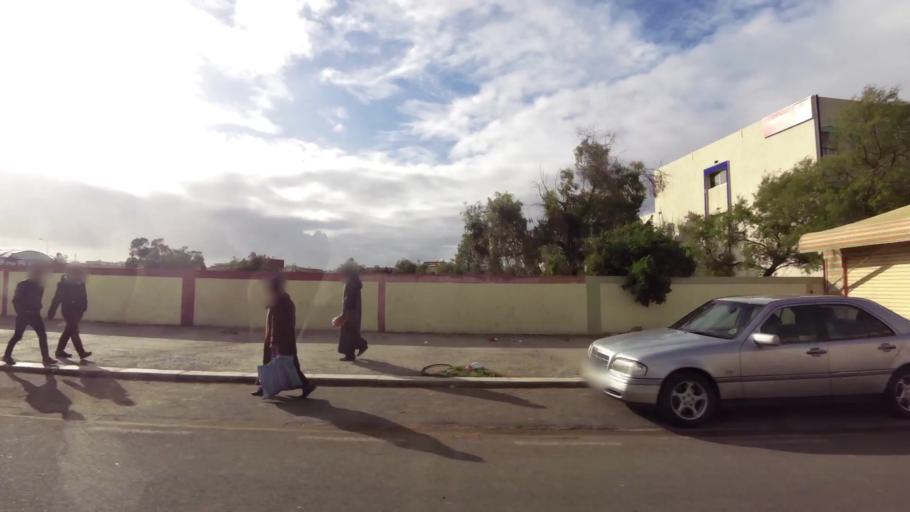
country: MA
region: Doukkala-Abda
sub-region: El-Jadida
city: El Jadida
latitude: 33.2460
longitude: -8.5194
